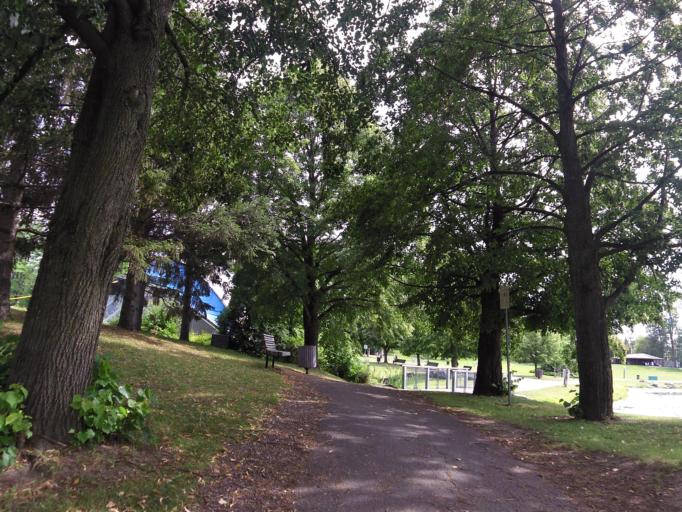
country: CA
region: Ontario
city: Bells Corners
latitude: 45.3510
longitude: -75.8198
